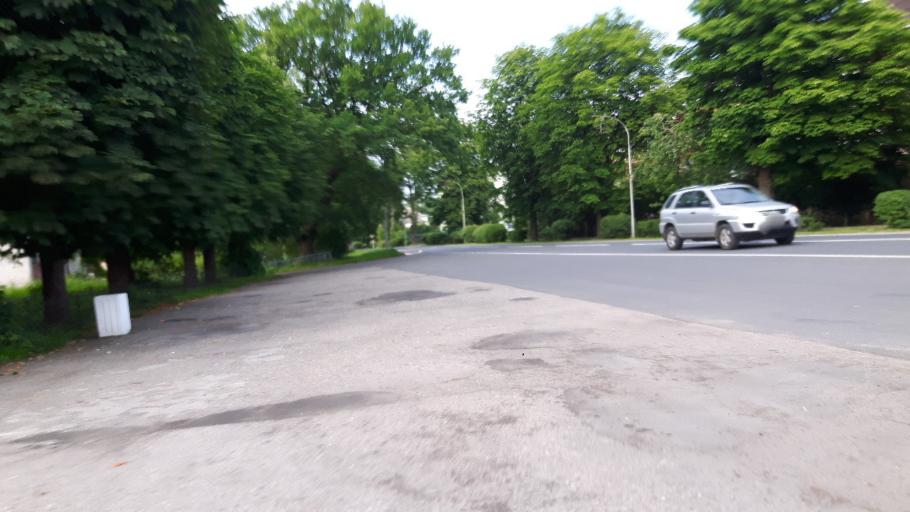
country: RU
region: Kaliningrad
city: Ladushkin
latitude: 54.5666
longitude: 20.1694
